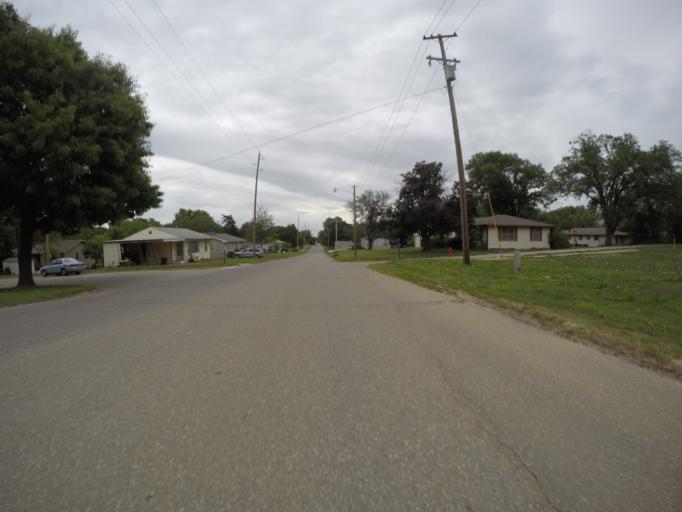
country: US
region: Kansas
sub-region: Pottawatomie County
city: Wamego
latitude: 39.2008
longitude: -96.3147
